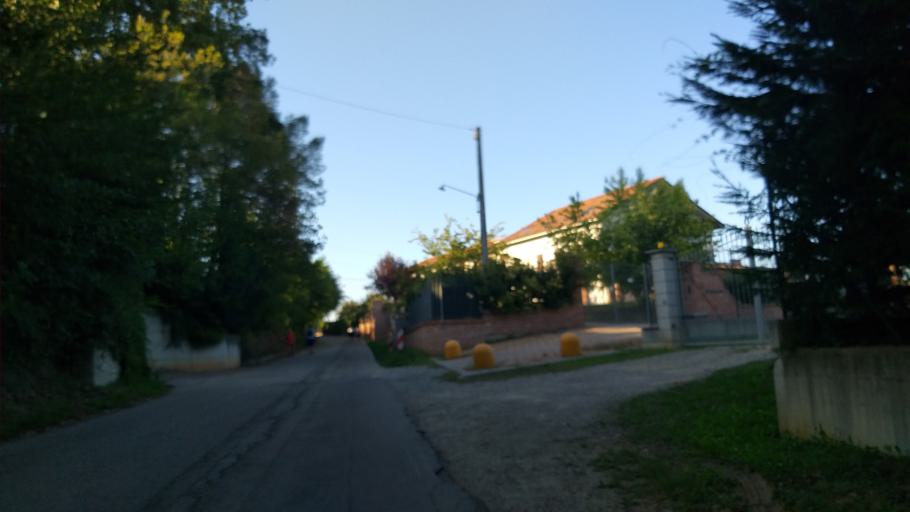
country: IT
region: Piedmont
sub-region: Provincia di Asti
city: Asti
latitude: 44.9209
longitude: 8.1998
